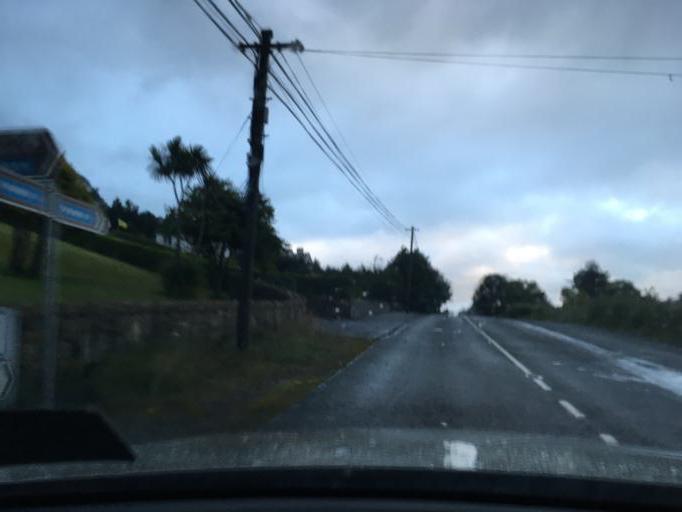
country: IE
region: Ulster
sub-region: County Donegal
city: Killybegs
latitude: 54.6377
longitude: -8.4898
